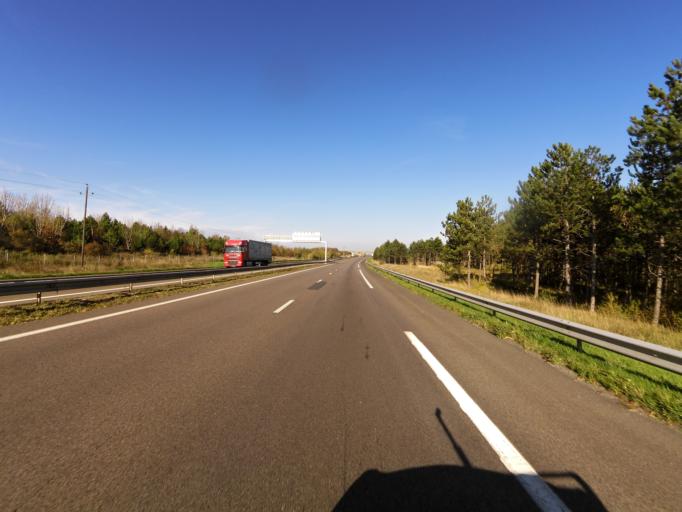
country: FR
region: Champagne-Ardenne
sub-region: Departement de la Marne
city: Verzy
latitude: 49.1346
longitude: 4.2209
